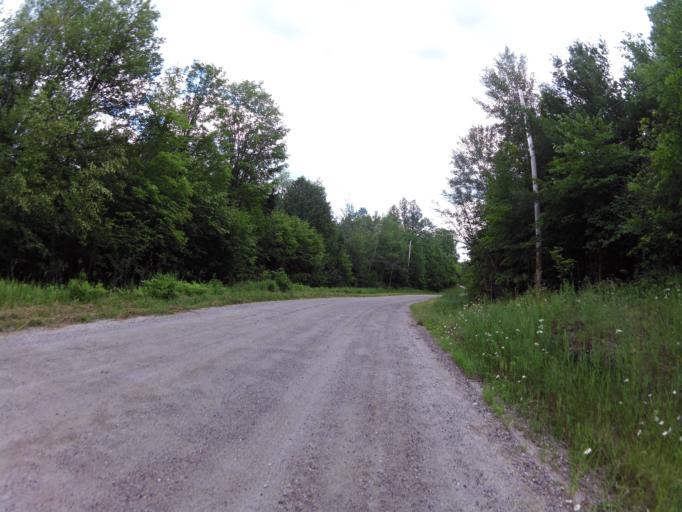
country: CA
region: Ontario
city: Perth
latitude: 45.0548
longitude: -76.4832
